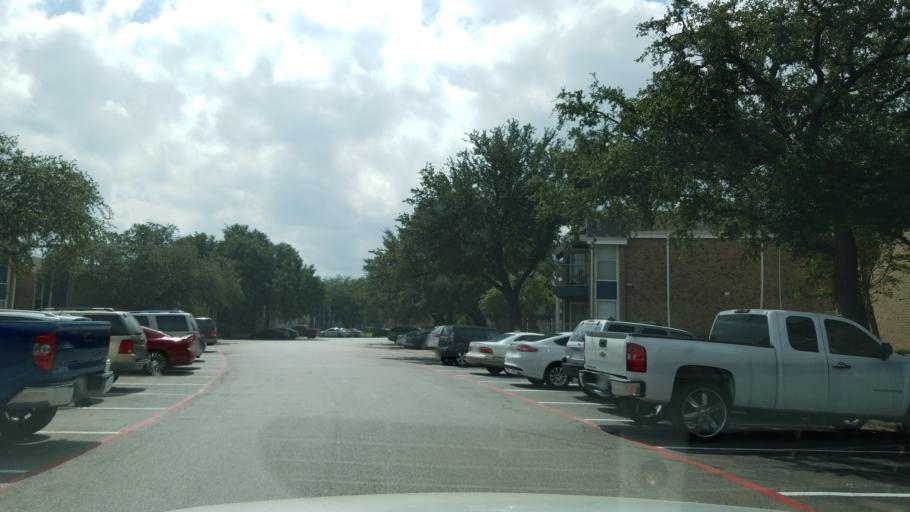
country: US
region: Texas
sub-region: Dallas County
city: Richardson
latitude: 32.9421
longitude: -96.7665
